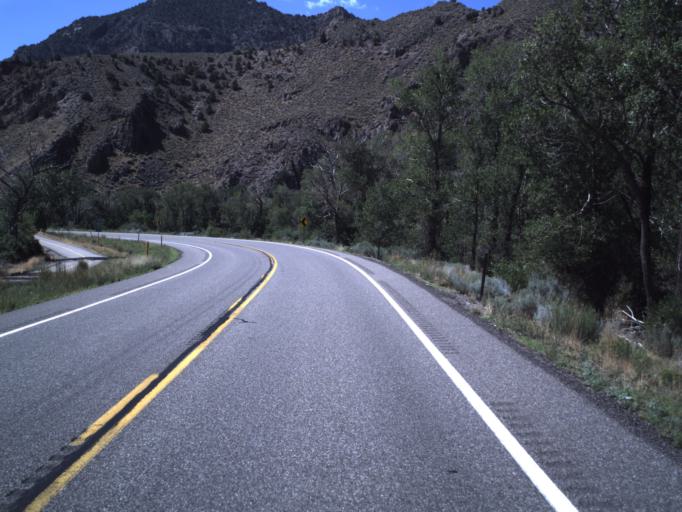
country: US
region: Utah
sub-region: Sevier County
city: Monroe
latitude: 38.5739
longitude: -112.2587
